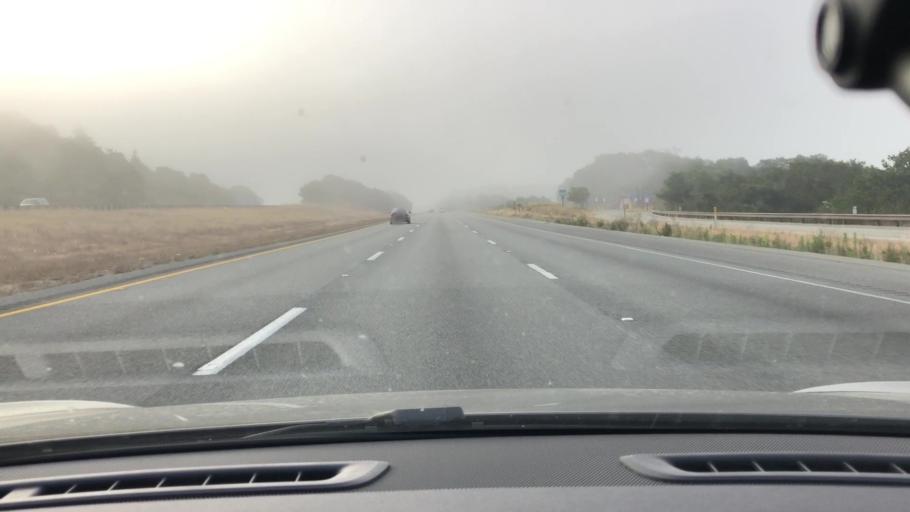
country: US
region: California
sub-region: Santa Cruz County
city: Aptos Hills-Larkin Valley
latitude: 36.9423
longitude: -121.8411
